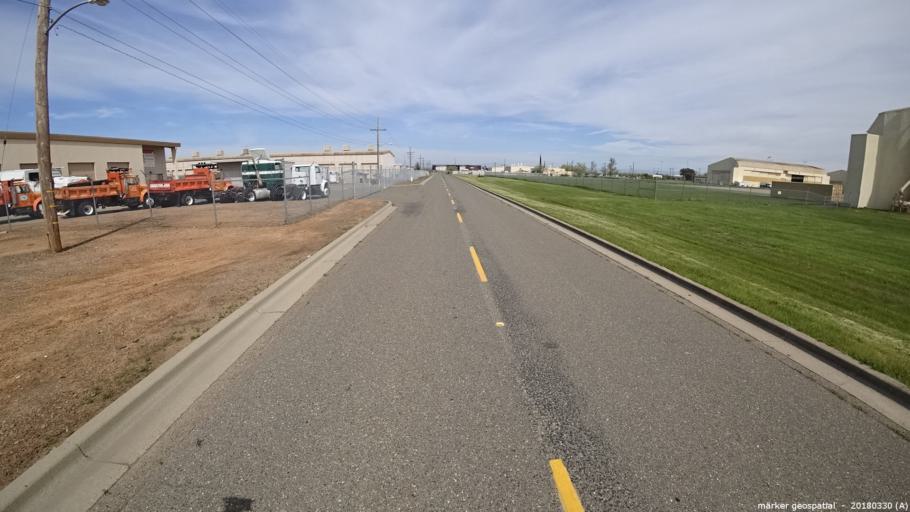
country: US
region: California
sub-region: Sacramento County
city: Rancho Cordova
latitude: 38.5577
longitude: -121.3155
